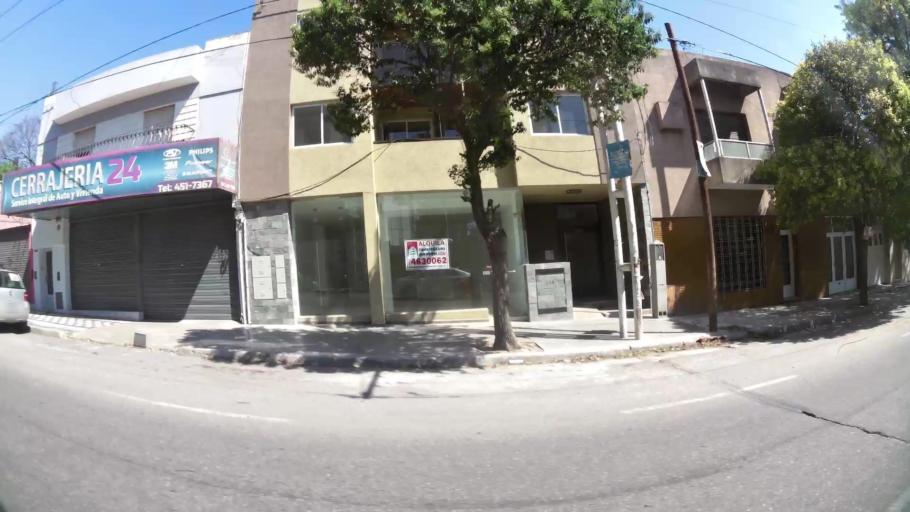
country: AR
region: Cordoba
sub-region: Departamento de Capital
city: Cordoba
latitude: -31.4117
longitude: -64.1582
